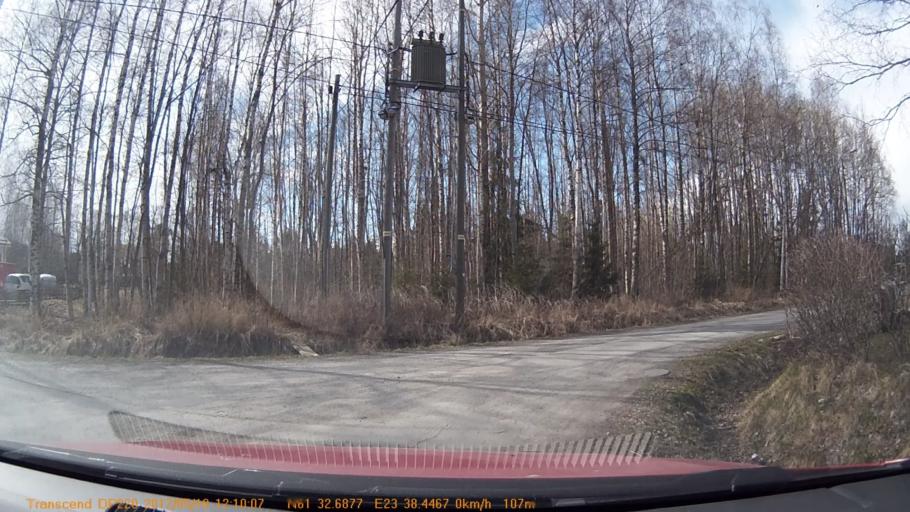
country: FI
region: Pirkanmaa
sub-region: Tampere
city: Yloejaervi
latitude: 61.5448
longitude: 23.6408
